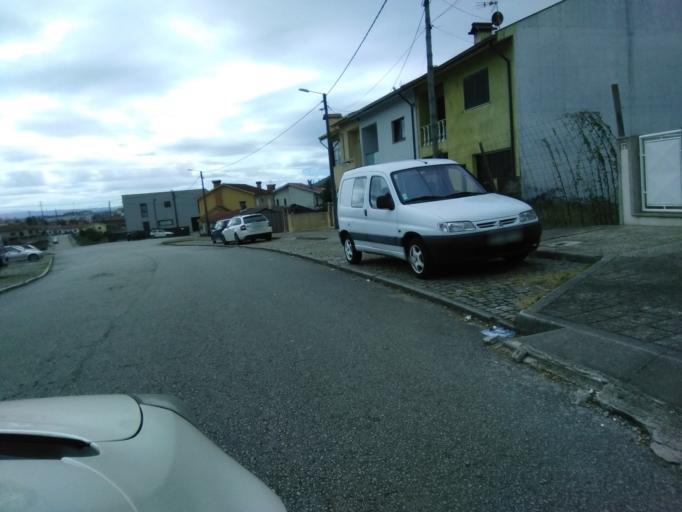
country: PT
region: Porto
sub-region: Valongo
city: Valongo
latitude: 41.1907
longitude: -8.4920
